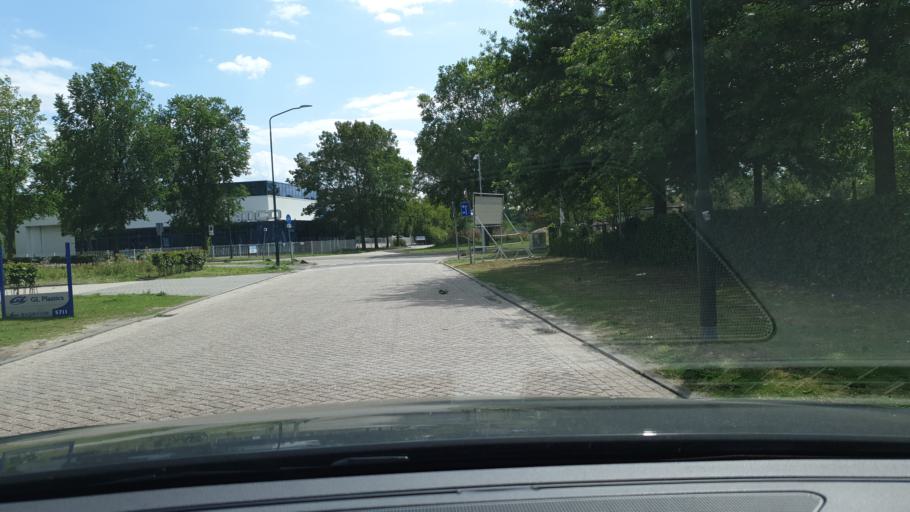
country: NL
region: North Brabant
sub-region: Gemeente Son en Breugel
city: Son
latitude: 51.4982
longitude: 5.4538
